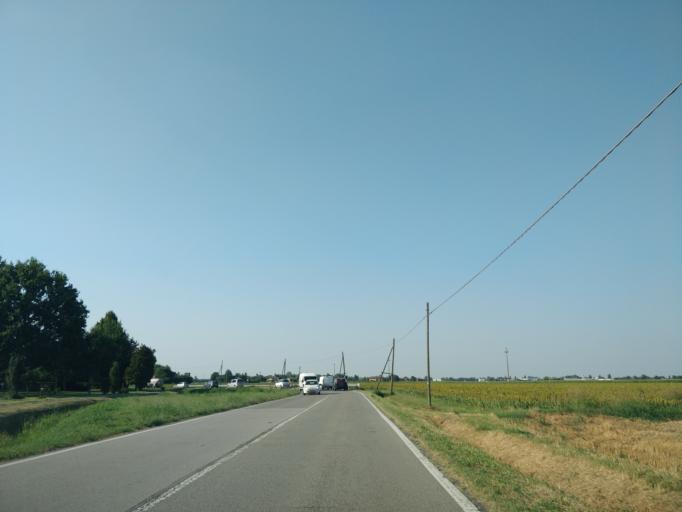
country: IT
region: Emilia-Romagna
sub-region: Provincia di Bologna
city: Argelato
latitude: 44.6177
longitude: 11.3377
